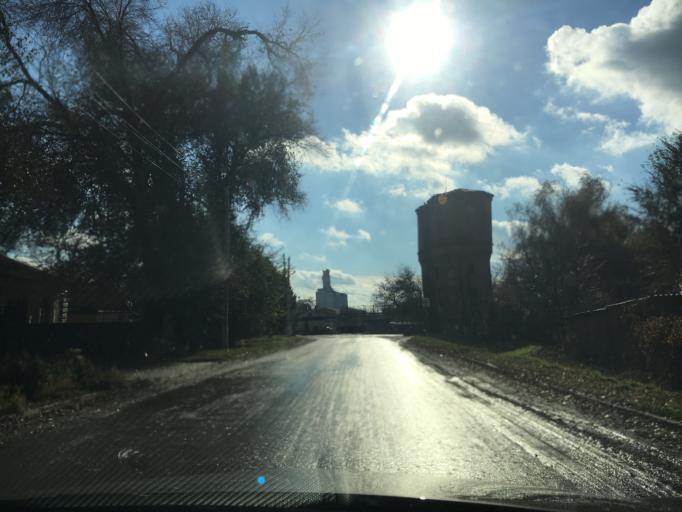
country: RU
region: Rostov
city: Matveyev Kurgan
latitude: 47.5631
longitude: 38.8618
